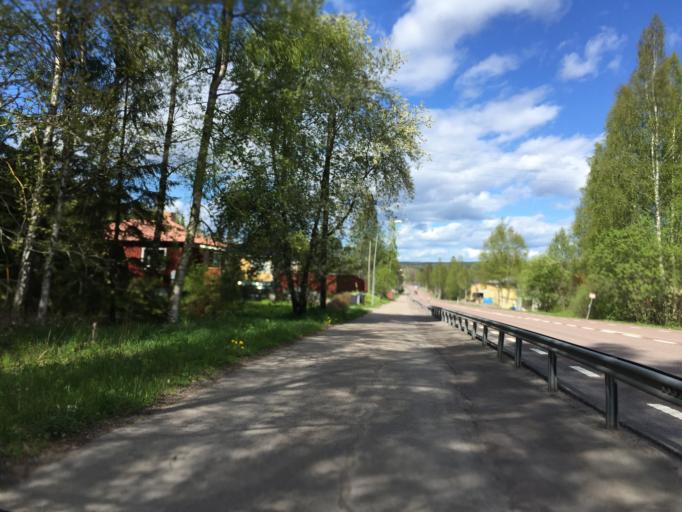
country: SE
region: Dalarna
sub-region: Ludvika Kommun
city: Ludvika
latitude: 60.1761
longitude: 15.2041
